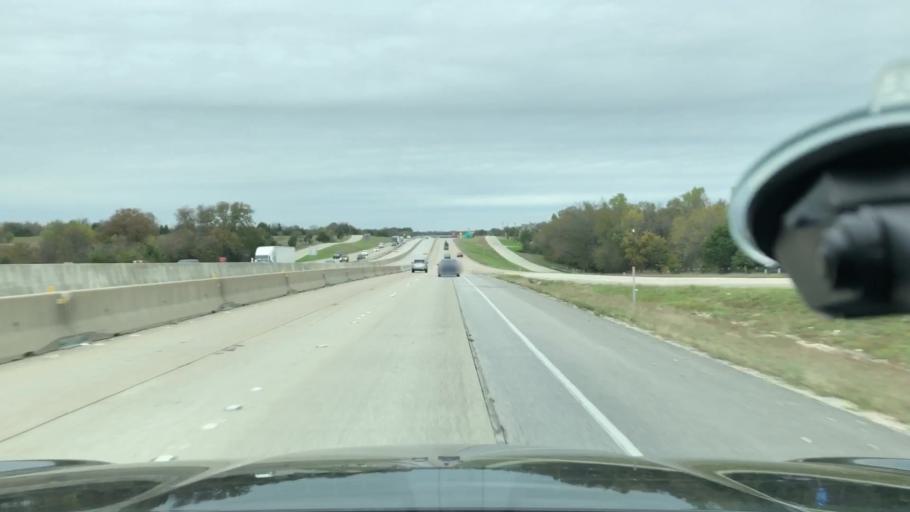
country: US
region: Texas
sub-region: Ellis County
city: Waxahachie
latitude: 32.3858
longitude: -96.8677
